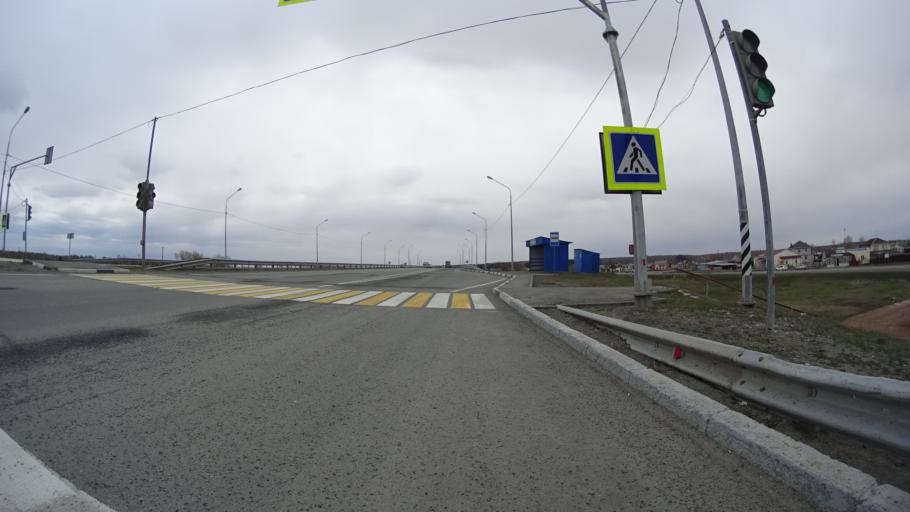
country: RU
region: Chelyabinsk
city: Yemanzhelinka
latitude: 54.7966
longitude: 61.3066
